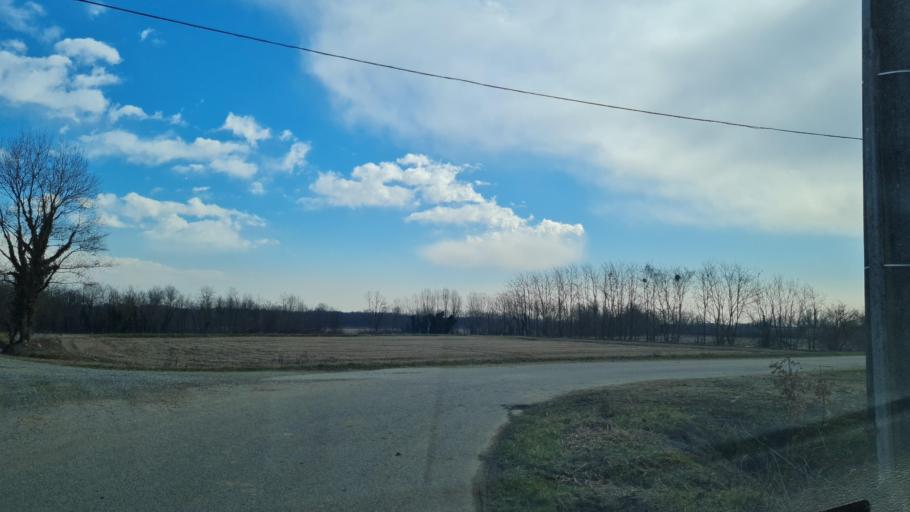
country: IT
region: Piedmont
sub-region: Provincia di Biella
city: Gifflenga
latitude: 45.4757
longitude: 8.2410
